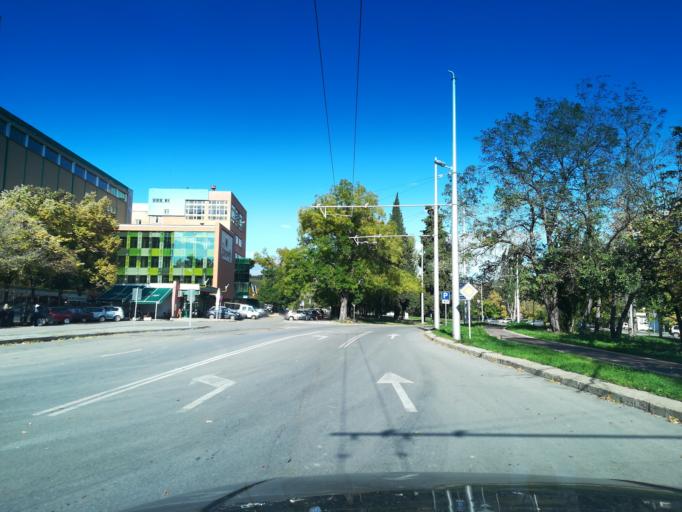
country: BG
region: Stara Zagora
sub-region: Obshtina Stara Zagora
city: Stara Zagora
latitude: 42.4424
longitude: 25.6338
